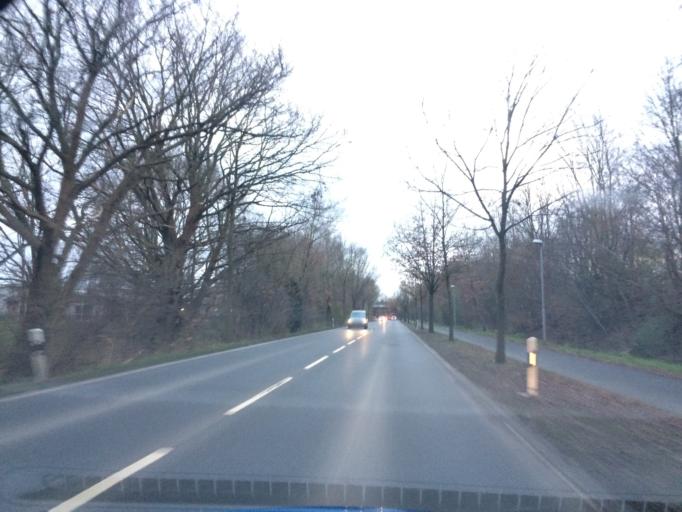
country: DE
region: Lower Saxony
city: Winsen
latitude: 53.3576
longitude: 10.2270
